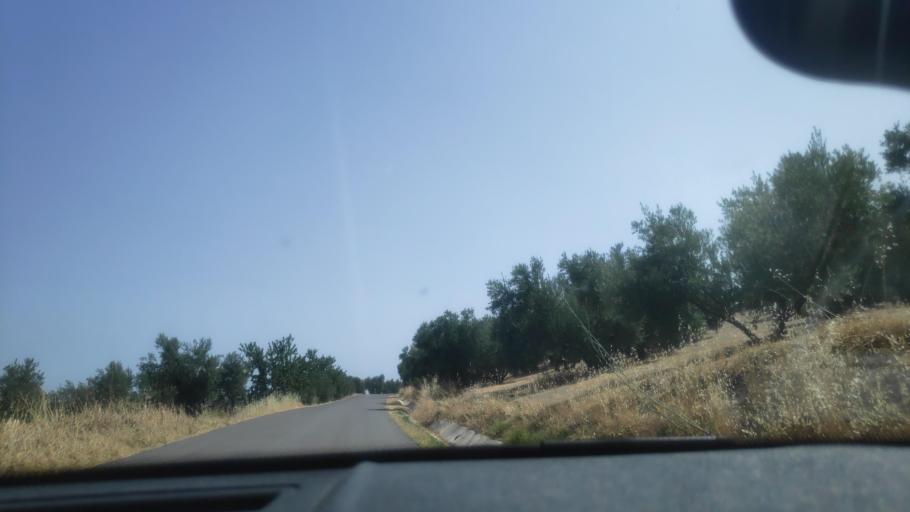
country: ES
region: Andalusia
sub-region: Provincia de Jaen
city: Jimena
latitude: 37.7915
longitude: -3.4523
